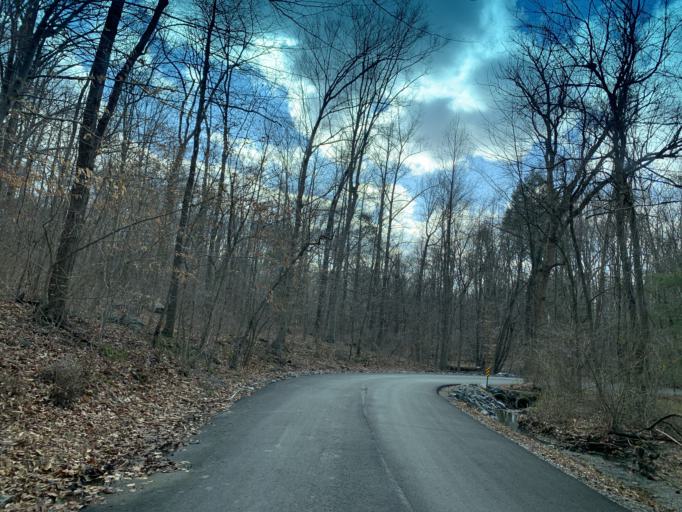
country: US
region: Maryland
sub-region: Harford County
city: Riverside
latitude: 39.5023
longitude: -76.2567
